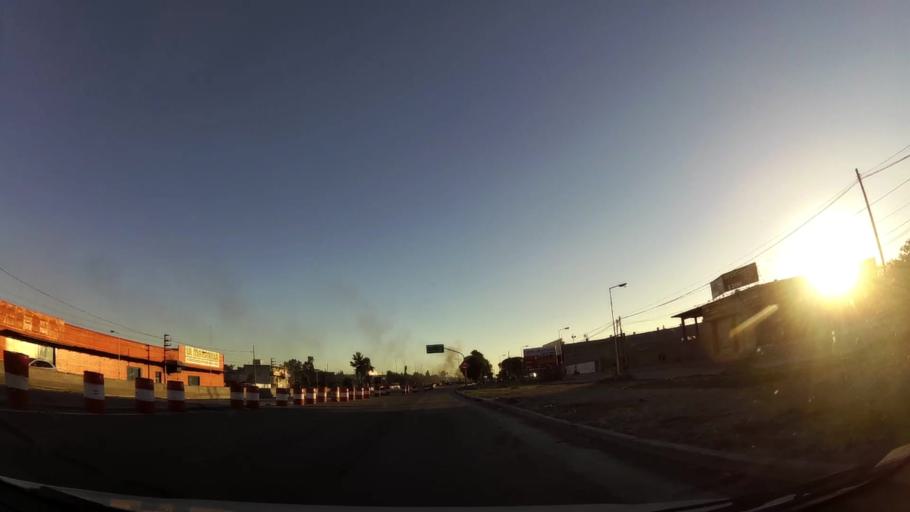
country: AR
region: Buenos Aires
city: San Justo
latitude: -34.7377
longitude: -58.6045
